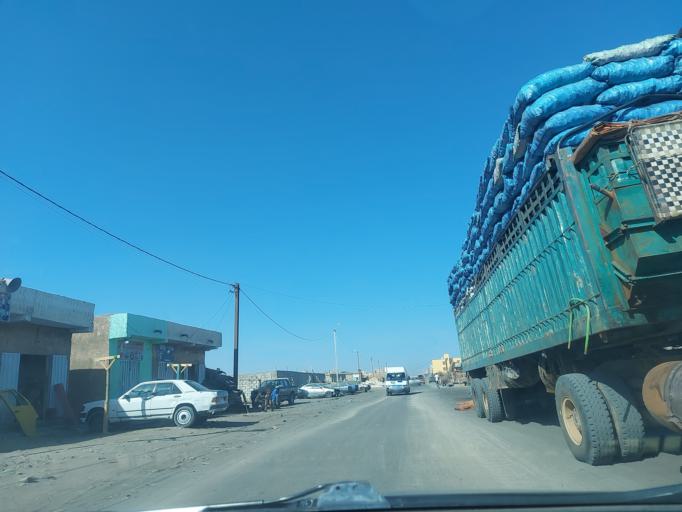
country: MR
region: Nouakchott
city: Nouakchott
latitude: 18.0680
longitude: -15.9948
